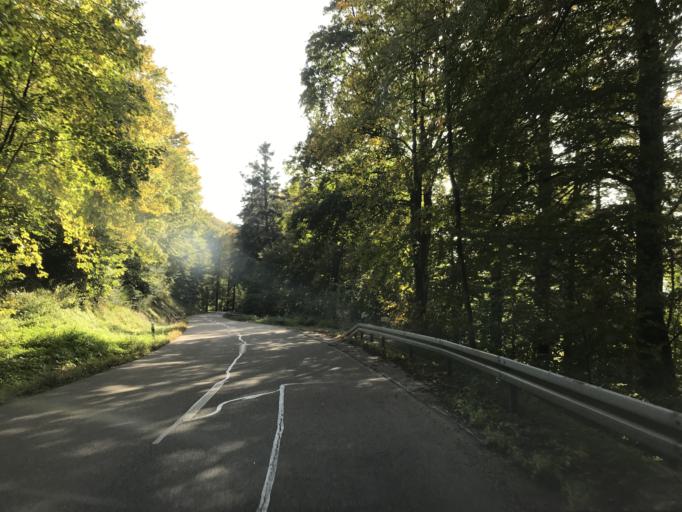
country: DE
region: Baden-Wuerttemberg
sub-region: Freiburg Region
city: Wehr
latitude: 47.6380
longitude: 7.9310
